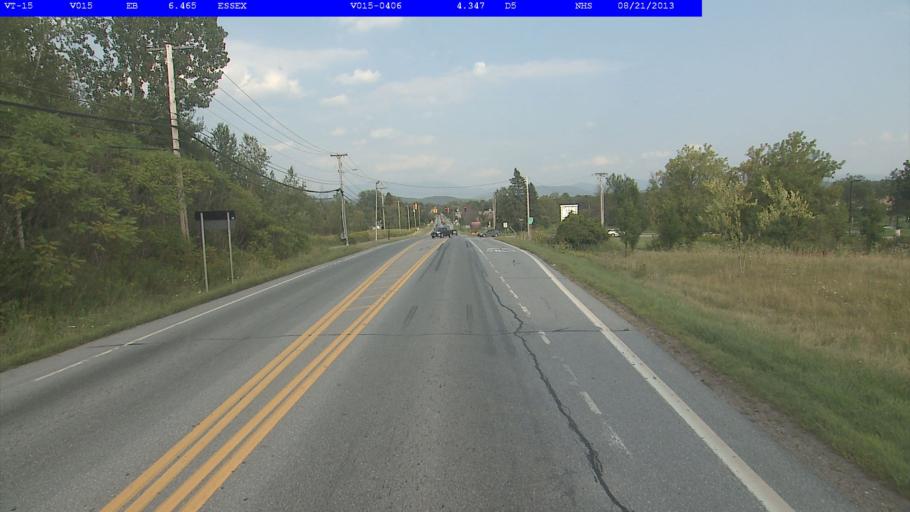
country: US
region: Vermont
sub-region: Chittenden County
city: Essex Junction
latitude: 44.5102
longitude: -73.0797
